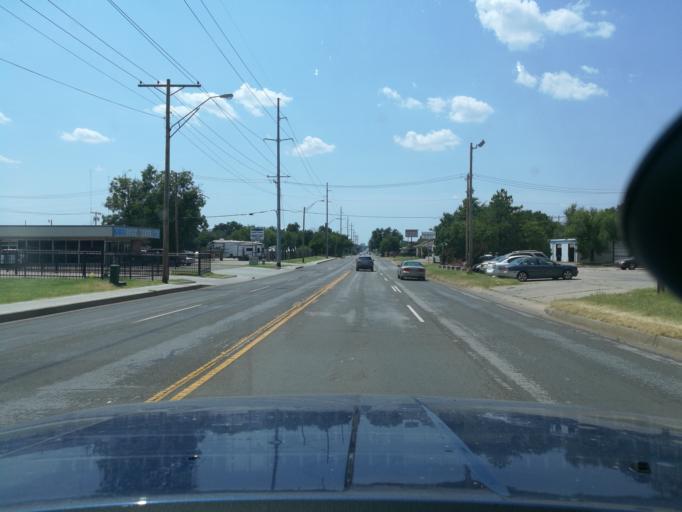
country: US
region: Oklahoma
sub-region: Oklahoma County
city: Oklahoma City
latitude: 35.4208
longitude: -97.4962
